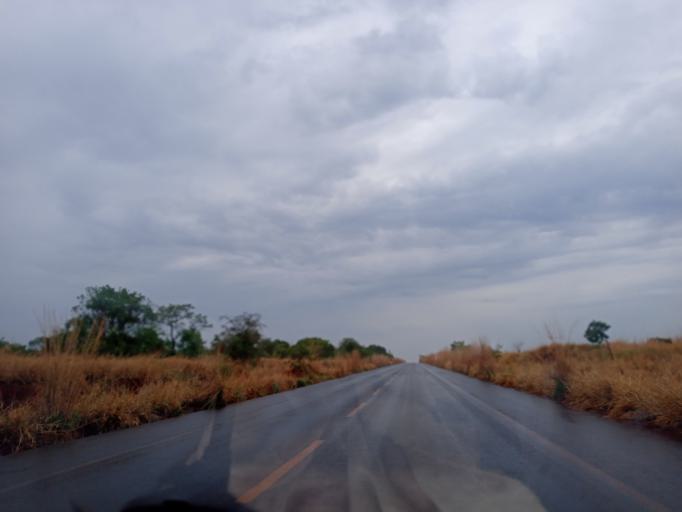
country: BR
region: Minas Gerais
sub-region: Ituiutaba
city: Ituiutaba
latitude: -19.1311
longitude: -49.5193
